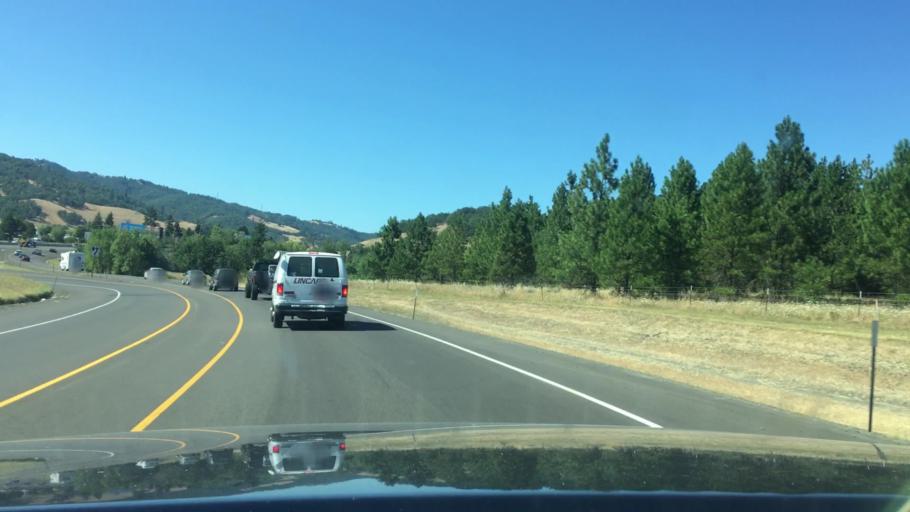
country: US
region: Oregon
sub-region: Douglas County
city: Green
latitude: 43.1559
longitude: -123.3630
